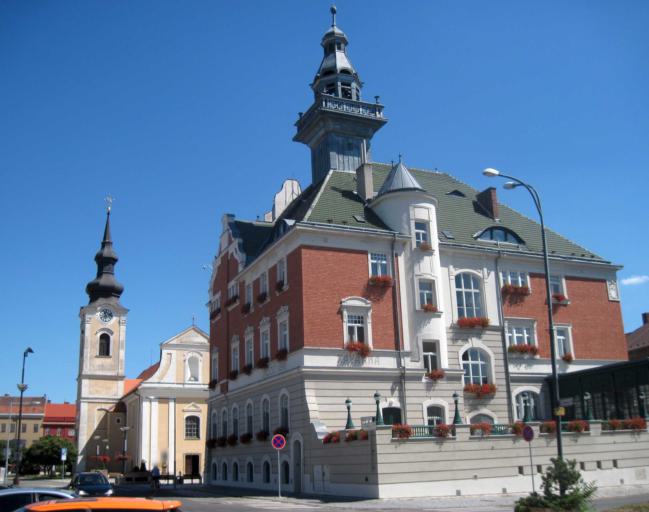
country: CZ
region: South Moravian
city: Hodonin
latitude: 48.8480
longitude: 17.1280
